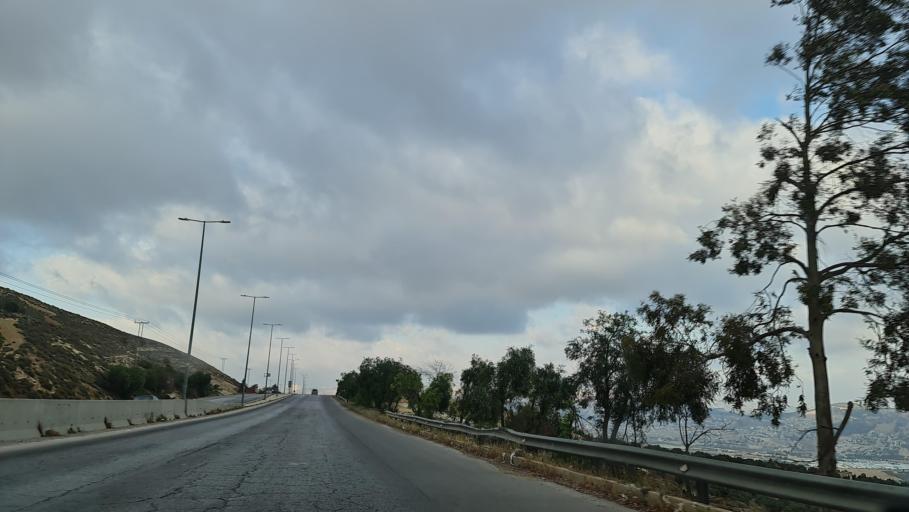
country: JO
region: Amman
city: Al Jubayhah
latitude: 32.0855
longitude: 35.8888
